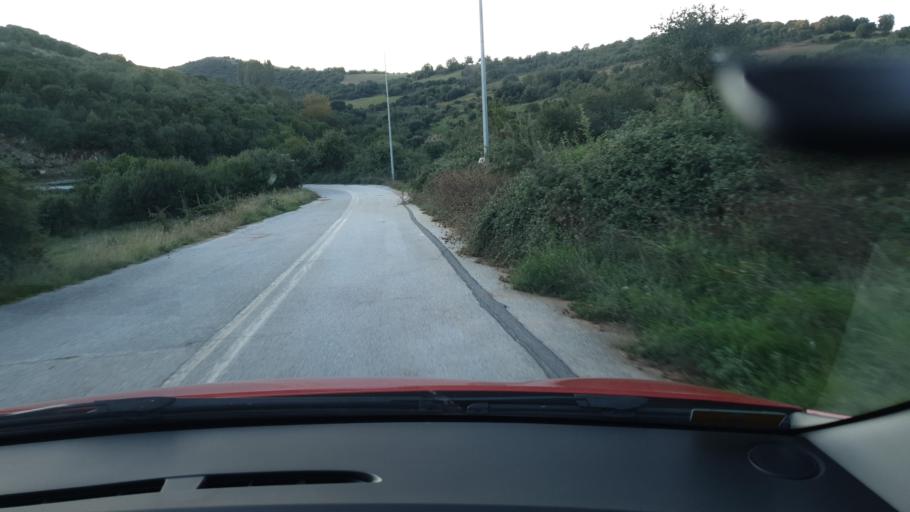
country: GR
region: Central Macedonia
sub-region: Nomos Chalkidikis
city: Galatista
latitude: 40.4621
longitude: 23.3228
